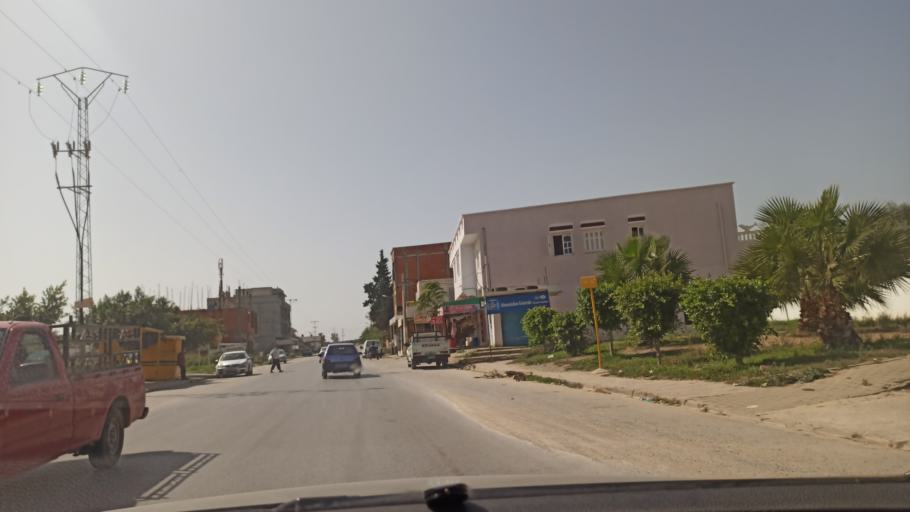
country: TN
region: Manouba
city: Manouba
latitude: 36.7550
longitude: 10.1023
